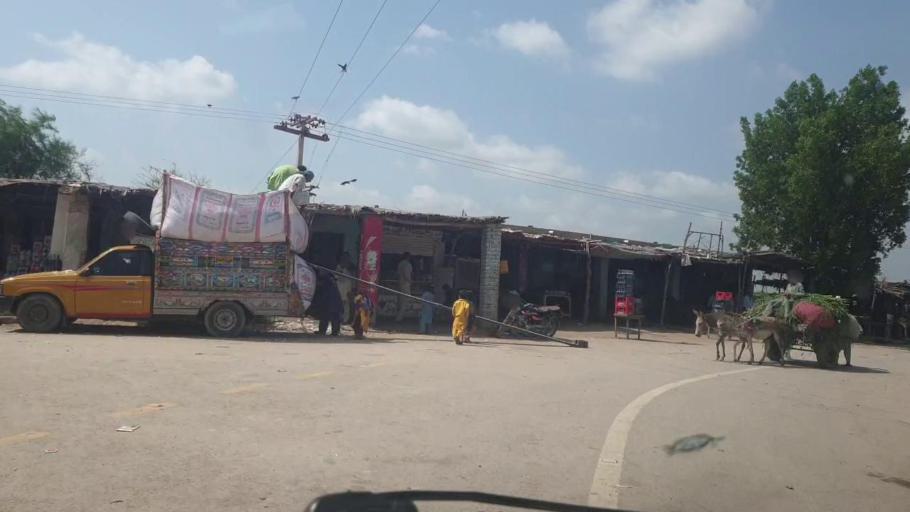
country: PK
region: Sindh
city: Berani
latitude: 25.6722
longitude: 68.9248
